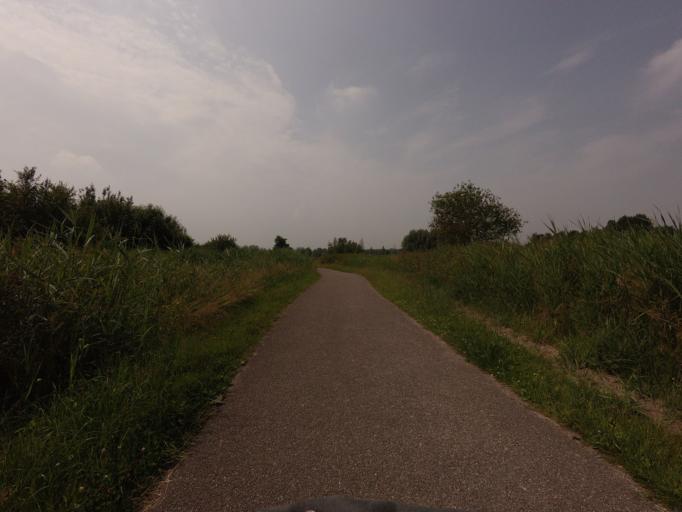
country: NL
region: South Holland
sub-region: Gemeente Krimpen aan den IJssel
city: Krimpen aan den IJssel
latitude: 51.9491
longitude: 4.6262
